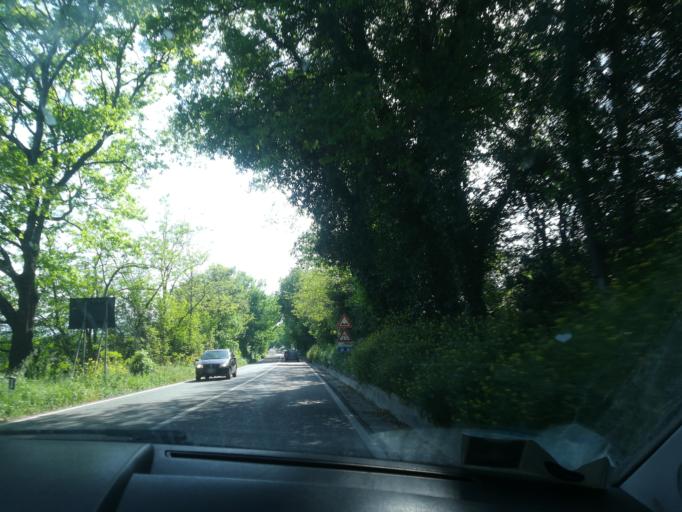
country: IT
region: The Marches
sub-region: Provincia di Macerata
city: Sforzacosta
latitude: 43.2747
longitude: 13.4307
